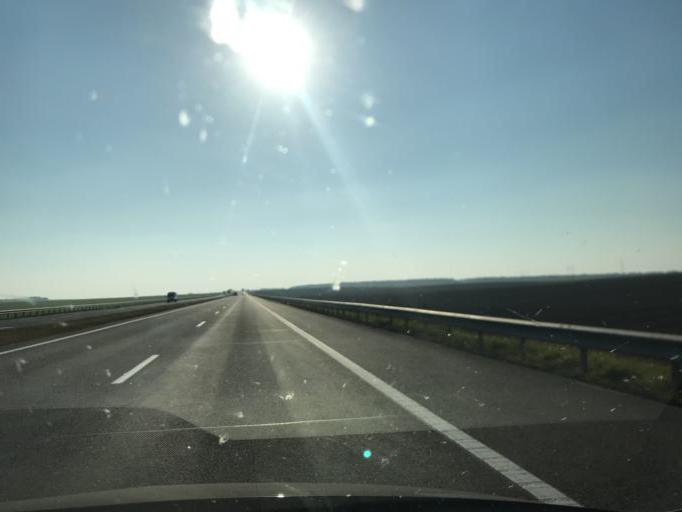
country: BY
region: Grodnenskaya
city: Mir
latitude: 53.4339
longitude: 26.5862
